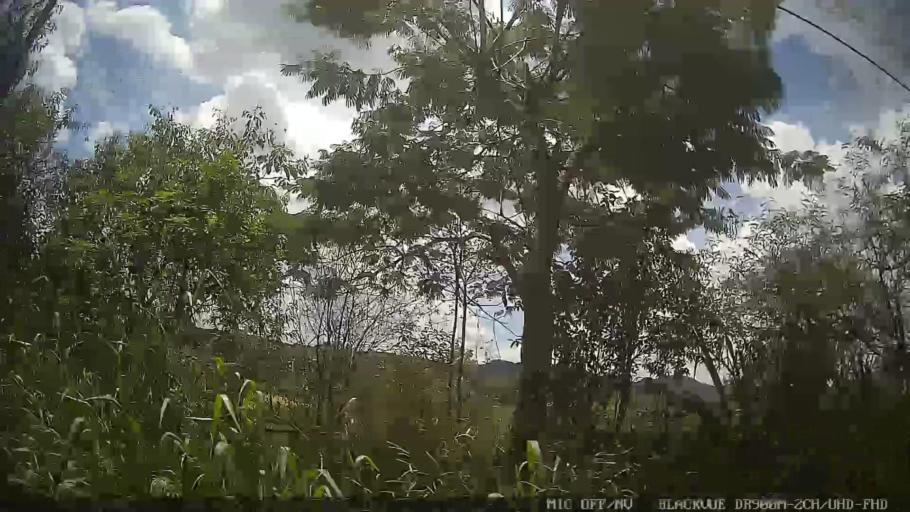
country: BR
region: Sao Paulo
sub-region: Atibaia
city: Atibaia
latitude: -23.1136
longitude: -46.5989
